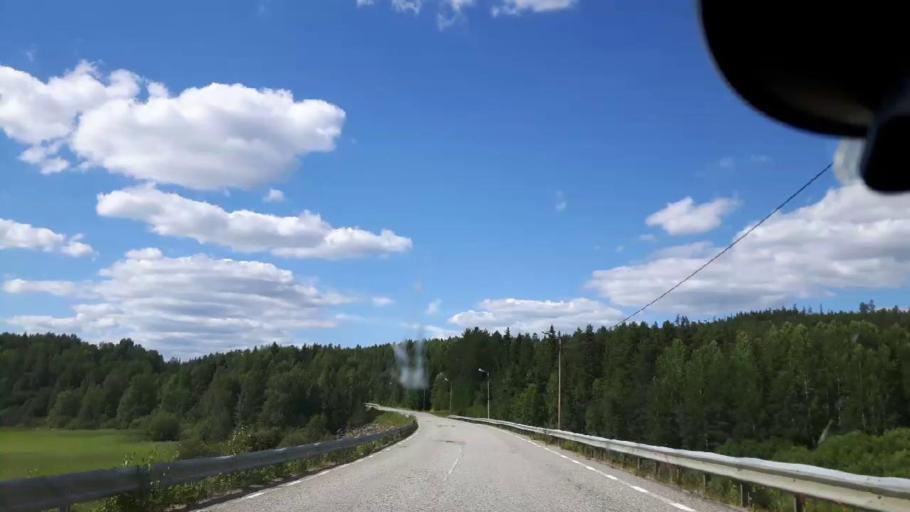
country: SE
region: Vaesternorrland
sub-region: Ange Kommun
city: Fransta
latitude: 62.7885
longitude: 16.2412
